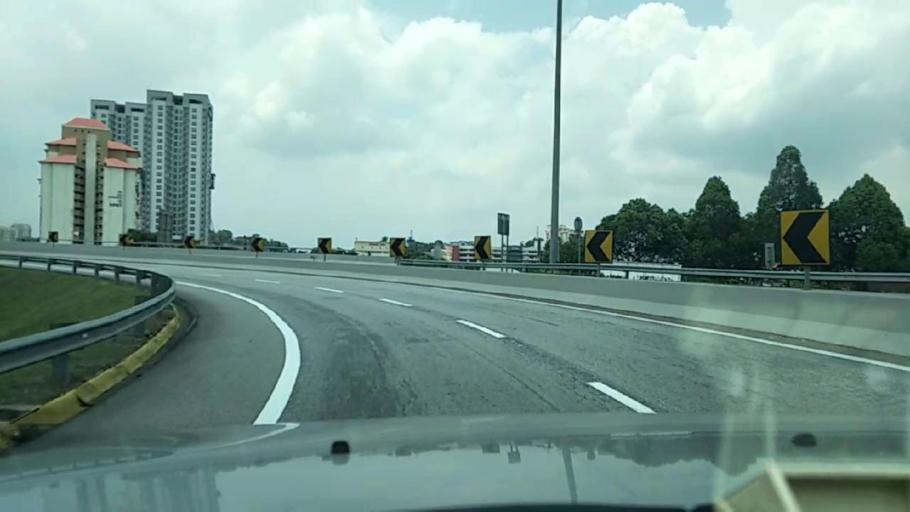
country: MY
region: Kuala Lumpur
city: Kuala Lumpur
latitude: 3.0915
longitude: 101.6706
